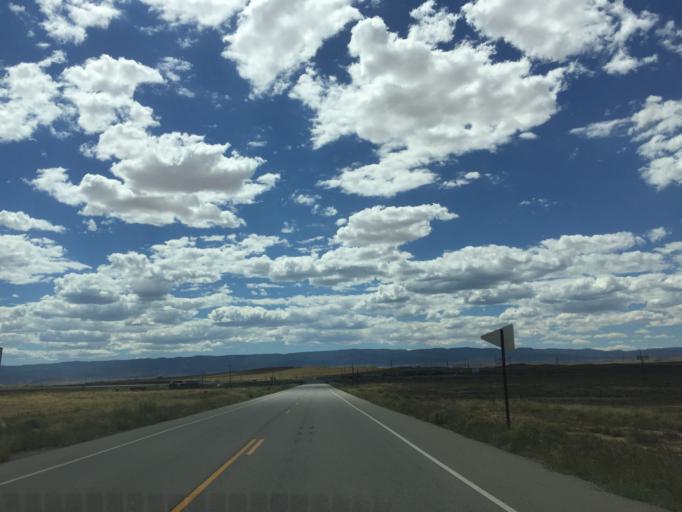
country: US
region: New Mexico
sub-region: San Juan County
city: Shiprock
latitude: 36.3359
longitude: -108.7076
